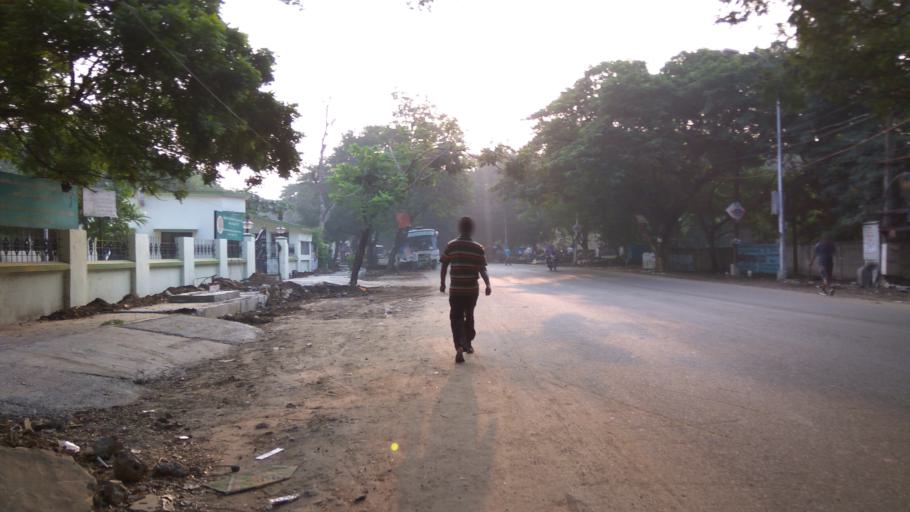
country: IN
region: Tamil Nadu
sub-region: Kancheepuram
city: Alandur
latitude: 13.0132
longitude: 80.2057
